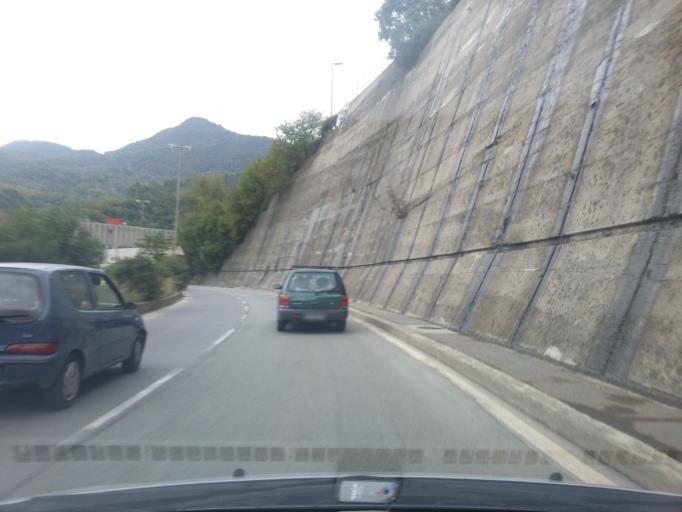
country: IT
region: Liguria
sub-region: Provincia di Genova
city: Piccarello
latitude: 44.4509
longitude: 8.9914
